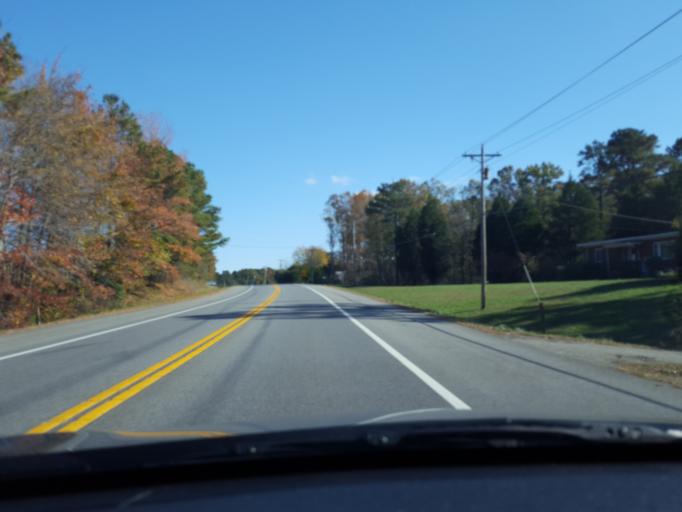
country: US
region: Maryland
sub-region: Saint Mary's County
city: California
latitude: 38.2393
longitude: -76.5541
